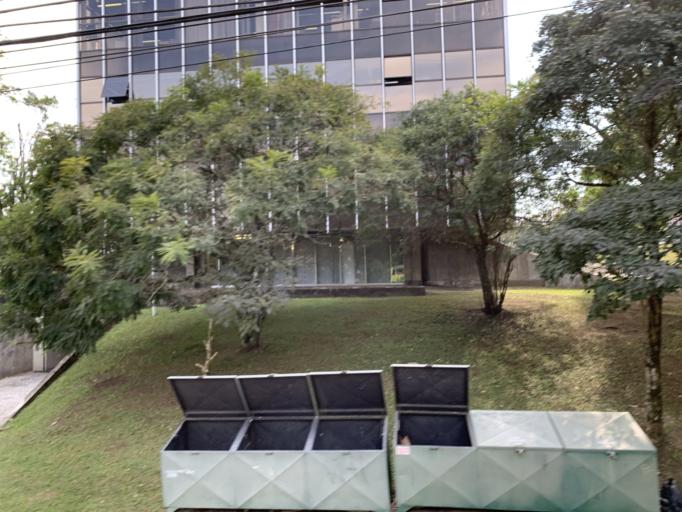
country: BR
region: Parana
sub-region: Curitiba
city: Curitiba
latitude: -25.4124
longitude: -49.2669
